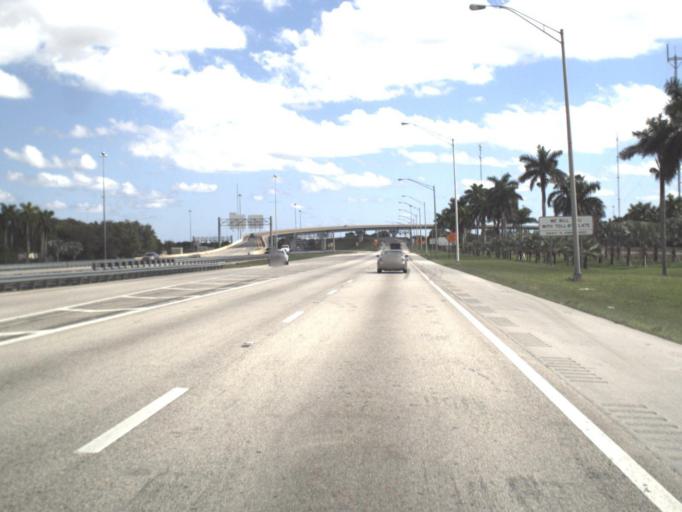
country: US
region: Florida
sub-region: Miami-Dade County
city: Lake Lucerne
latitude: 25.9725
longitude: -80.2377
